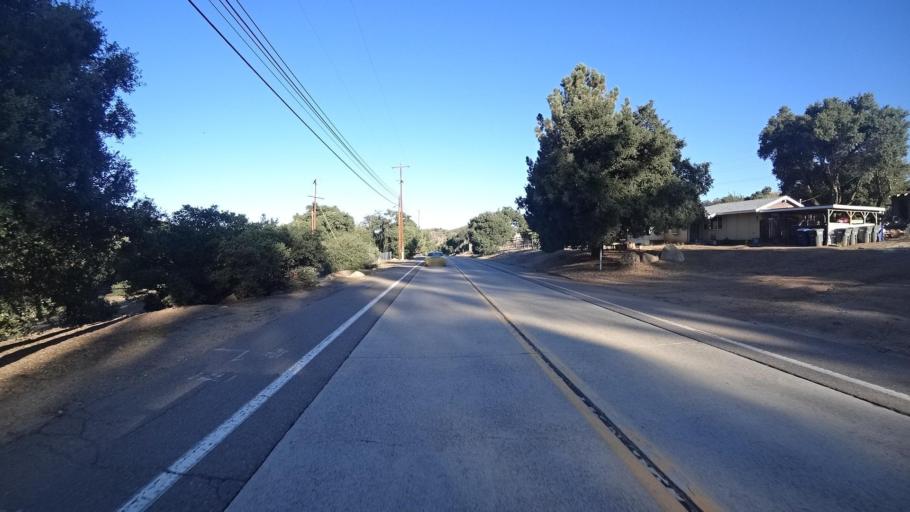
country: US
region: California
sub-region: San Diego County
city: Pine Valley
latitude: 32.8497
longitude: -116.5618
